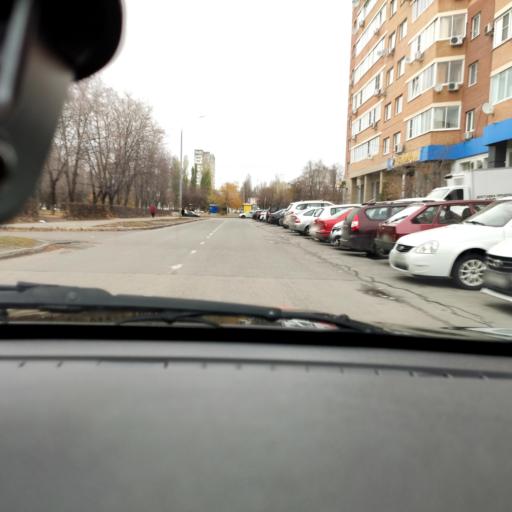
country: RU
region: Samara
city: Tol'yatti
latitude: 53.5164
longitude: 49.3025
